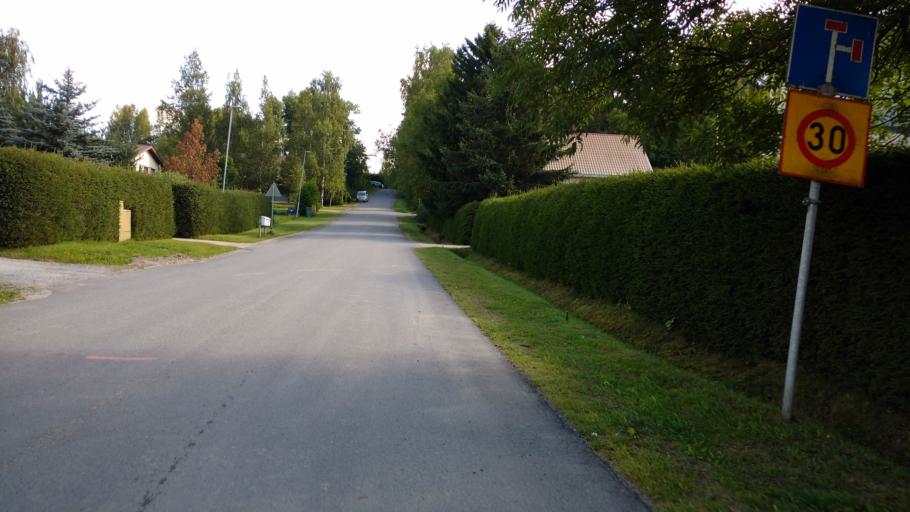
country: FI
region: Varsinais-Suomi
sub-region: Salo
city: Salo
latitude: 60.3729
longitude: 23.1709
